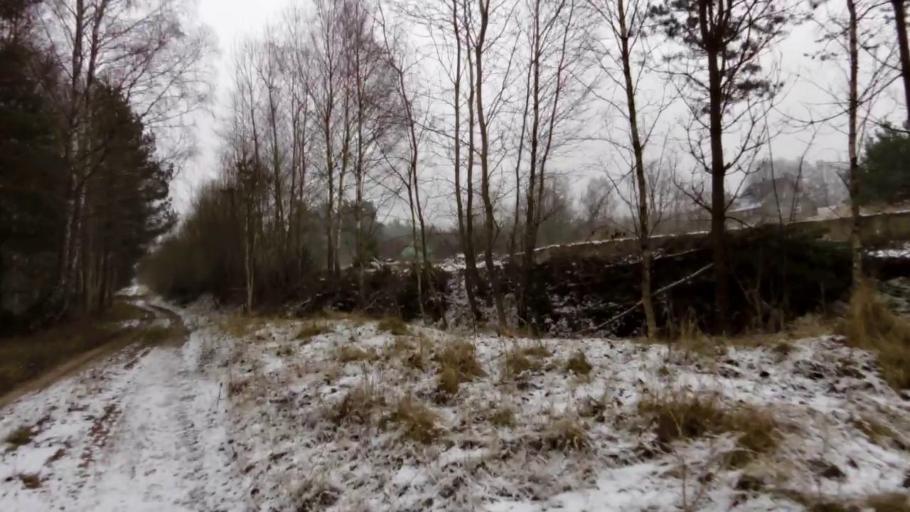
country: PL
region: West Pomeranian Voivodeship
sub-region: Powiat drawski
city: Wierzchowo
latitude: 53.4425
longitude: 16.2047
